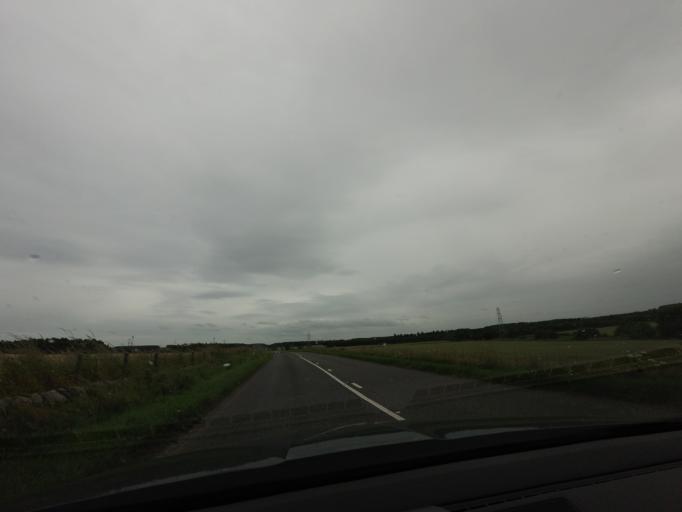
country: GB
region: Scotland
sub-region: Aberdeenshire
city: Portsoy
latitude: 57.6706
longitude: -2.6808
